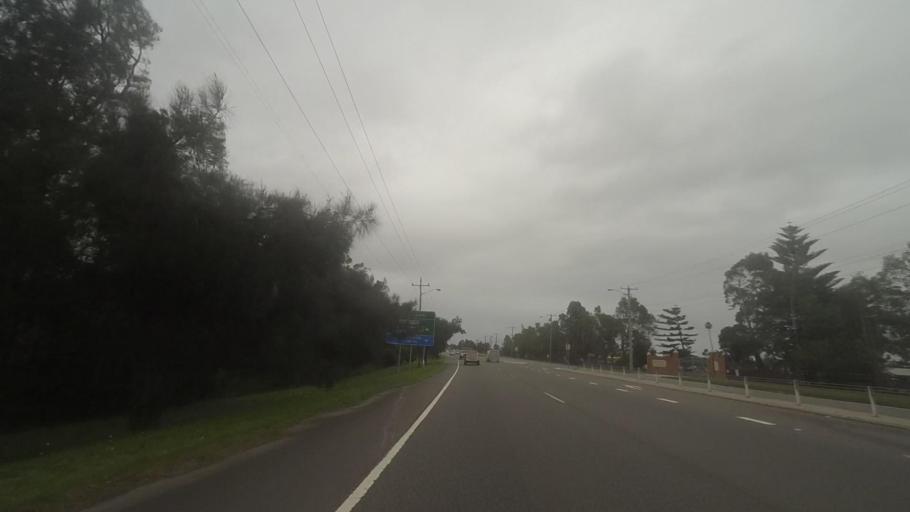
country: AU
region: New South Wales
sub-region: Newcastle
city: Mayfield West
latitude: -32.8673
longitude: 151.7080
